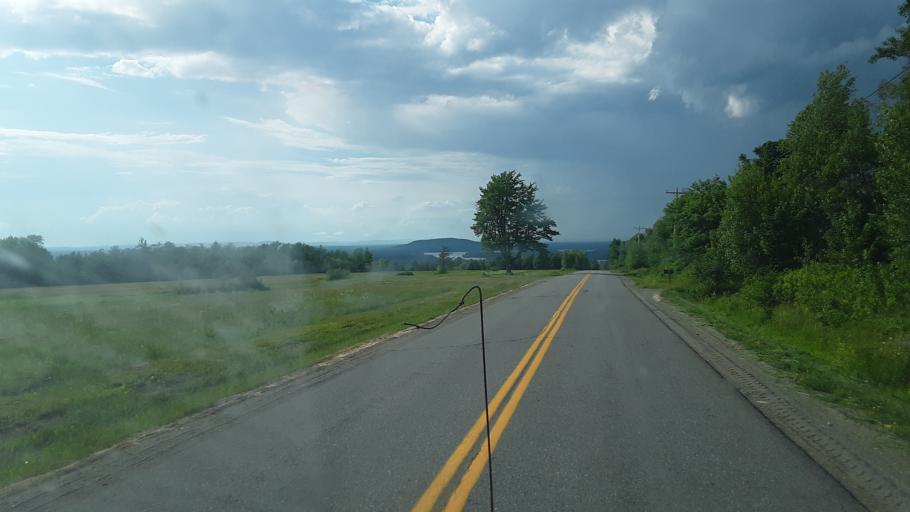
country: US
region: Maine
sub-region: Washington County
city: Calais
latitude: 45.0936
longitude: -67.5067
